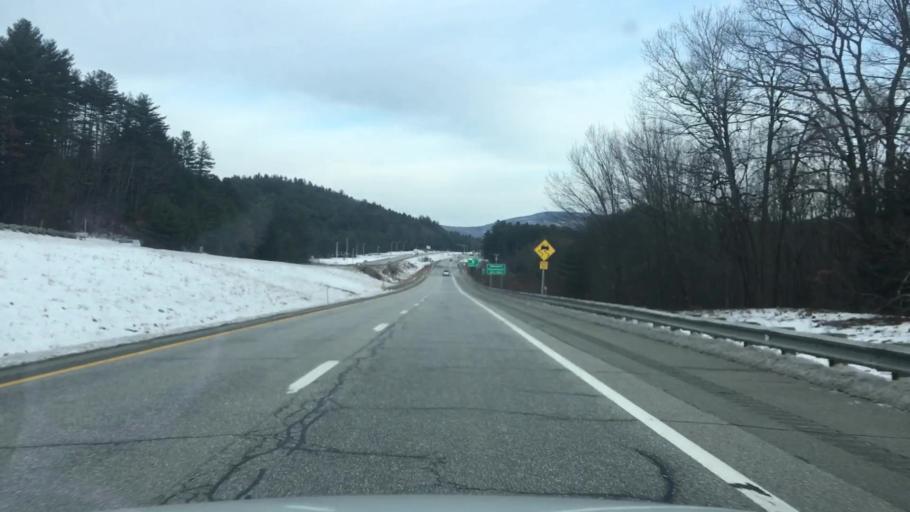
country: US
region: New Hampshire
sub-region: Merrimack County
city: Henniker
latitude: 43.2854
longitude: -71.8341
